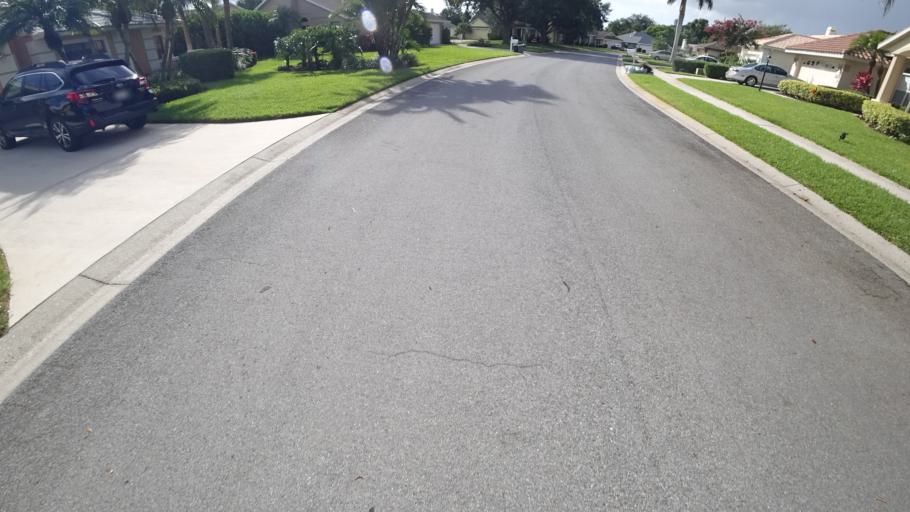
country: US
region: Florida
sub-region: Sarasota County
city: Desoto Lakes
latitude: 27.4186
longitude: -82.4859
